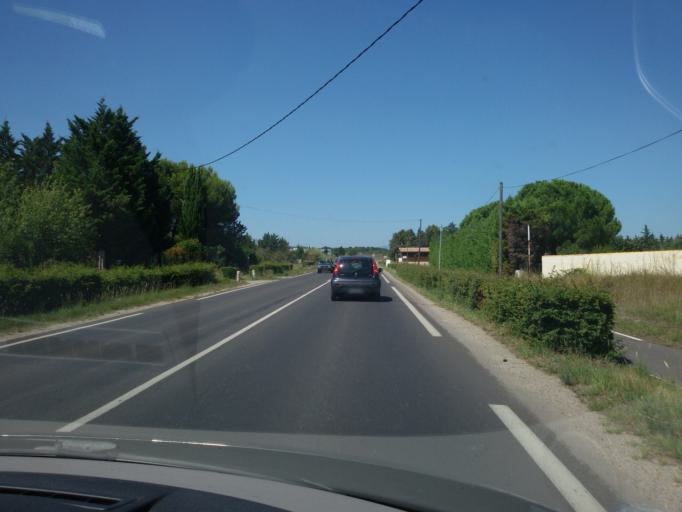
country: FR
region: Languedoc-Roussillon
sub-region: Departement de l'Herault
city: Villeneuve-les-Maguelone
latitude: 43.5405
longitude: 3.8515
